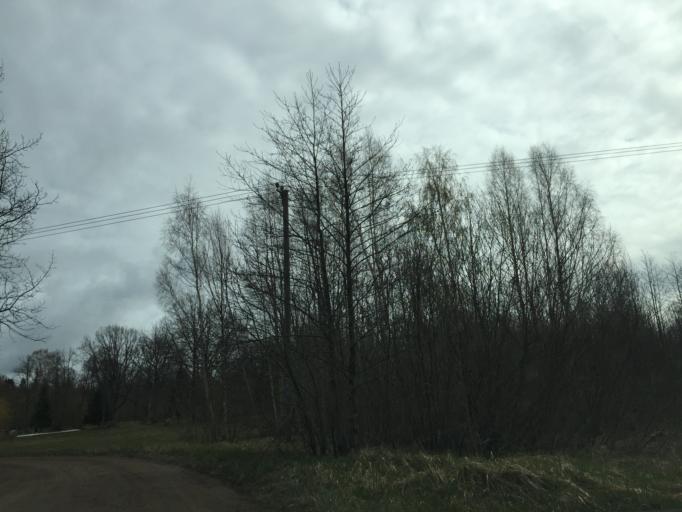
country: LV
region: Salacgrivas
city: Salacgriva
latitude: 57.5237
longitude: 24.3803
